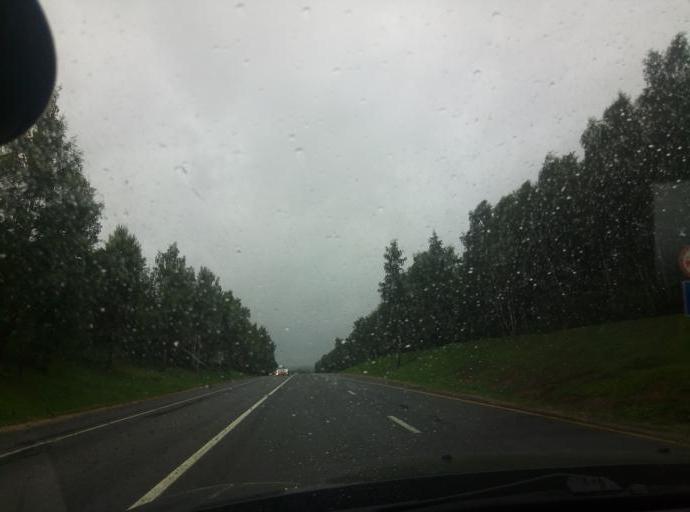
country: RU
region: Tula
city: Barsuki
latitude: 54.2825
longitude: 37.5373
